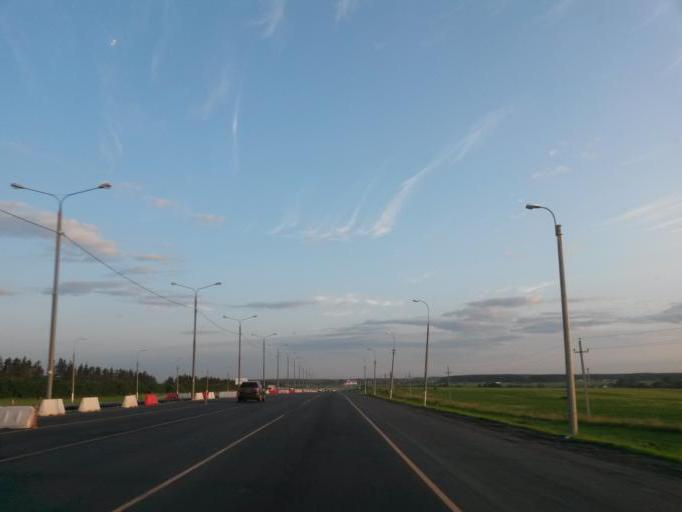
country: RU
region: Moskovskaya
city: Klimovsk
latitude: 55.3581
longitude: 37.5972
